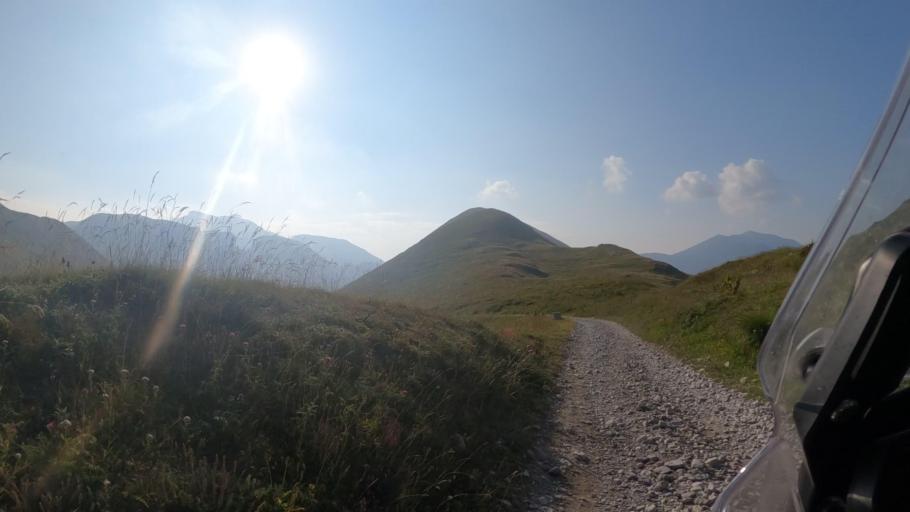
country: IT
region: Piedmont
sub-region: Provincia di Cuneo
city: Limone Piemonte
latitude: 44.1638
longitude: 7.6293
